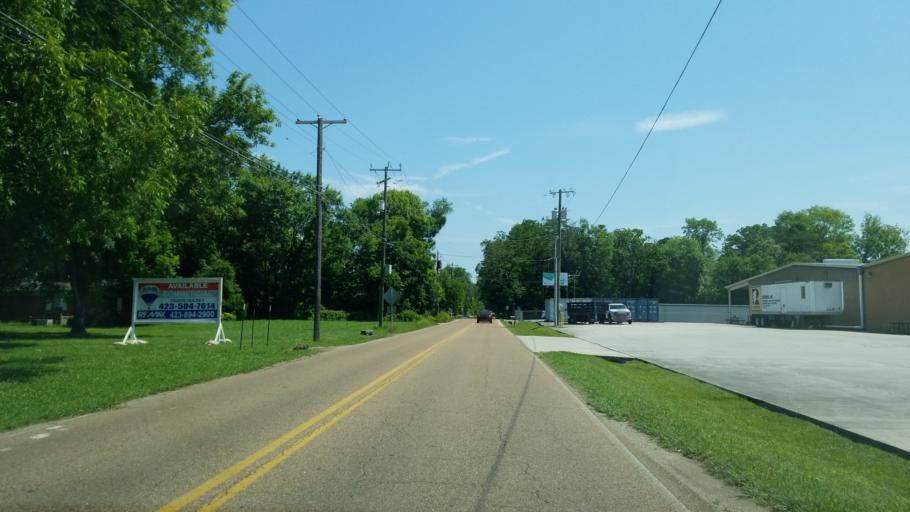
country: US
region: Tennessee
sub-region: Hamilton County
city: Collegedale
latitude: 35.0850
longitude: -85.0573
